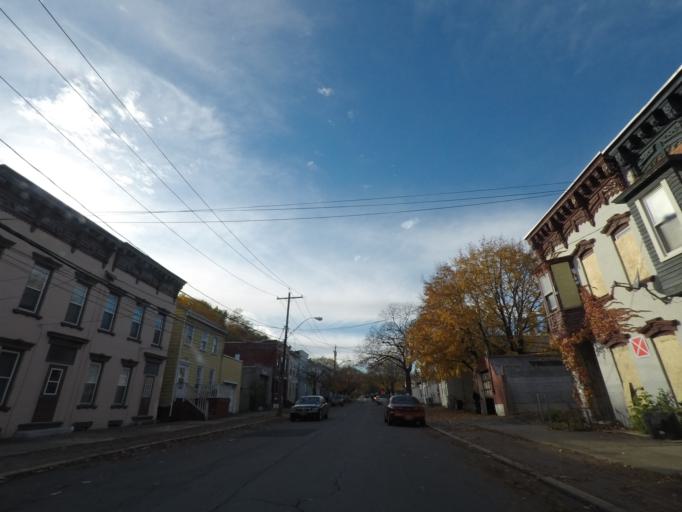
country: US
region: New York
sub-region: Albany County
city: Albany
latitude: 42.6353
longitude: -73.7624
